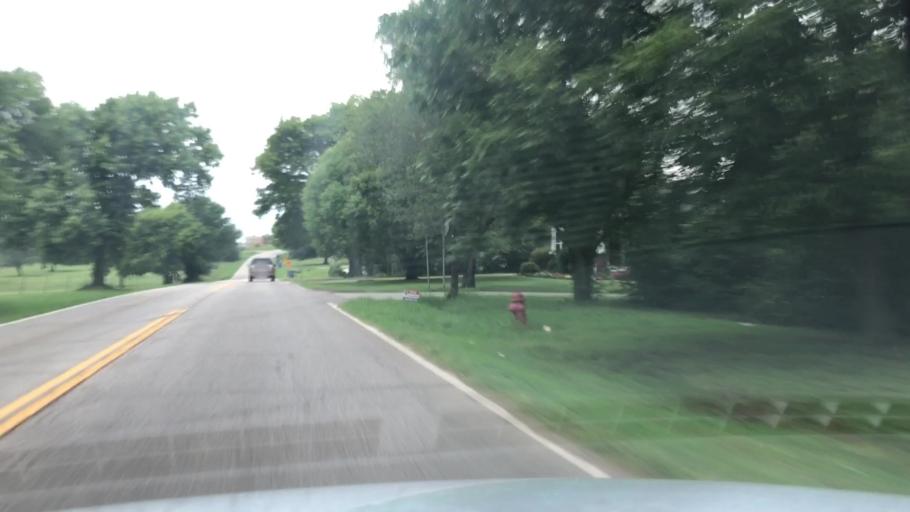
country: US
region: Oklahoma
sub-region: Nowata County
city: Nowata
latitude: 36.7027
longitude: -95.6440
